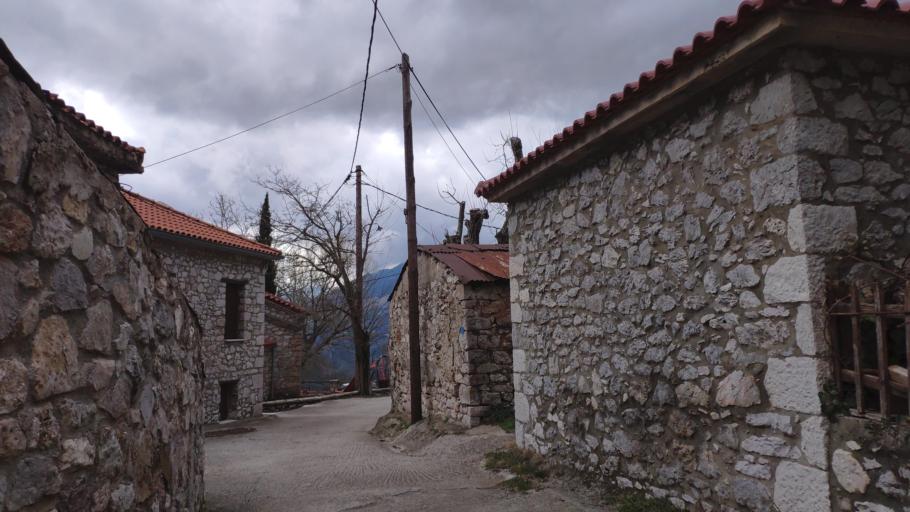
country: GR
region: Central Greece
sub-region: Nomos Fokidos
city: Amfissa
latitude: 38.6430
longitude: 22.4242
